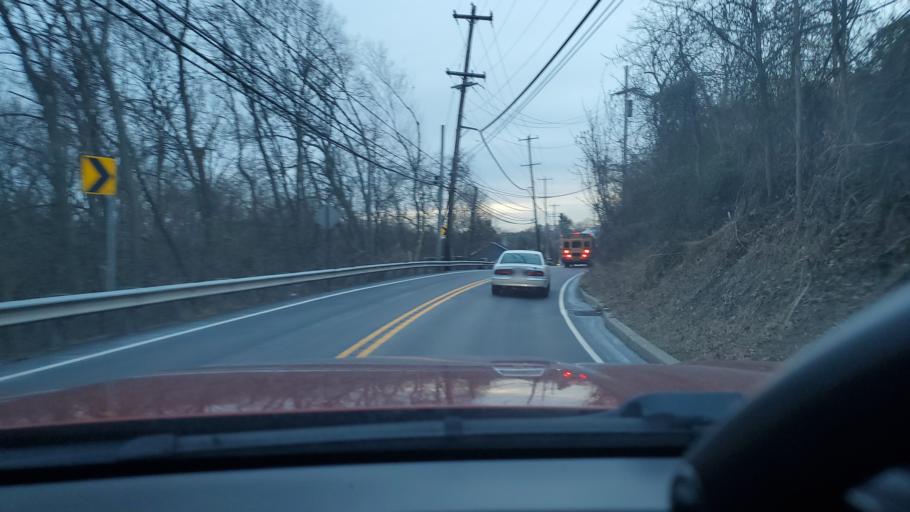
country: US
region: Pennsylvania
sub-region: Montgomery County
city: Schwenksville
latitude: 40.2427
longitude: -75.4562
